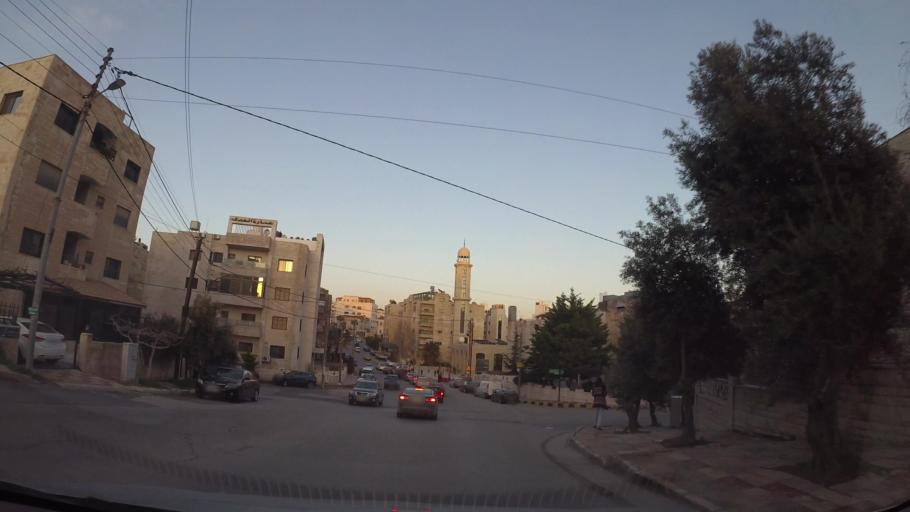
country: JO
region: Amman
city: Al Jubayhah
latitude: 31.9985
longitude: 35.8631
